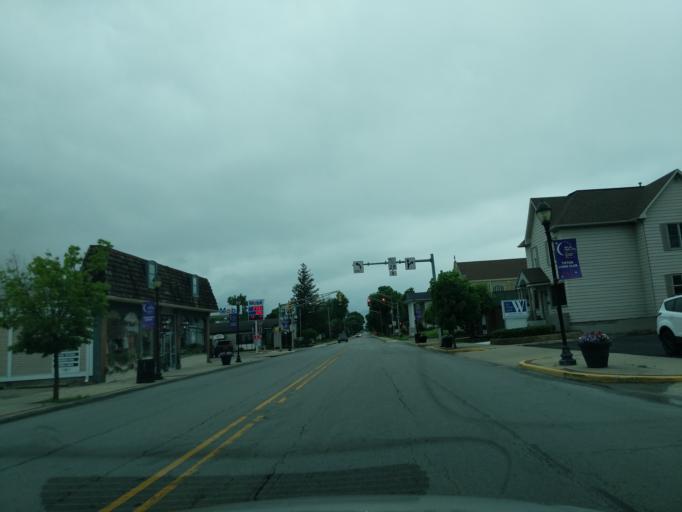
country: US
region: Indiana
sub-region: Tipton County
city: Tipton
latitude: 40.2822
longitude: -86.0420
